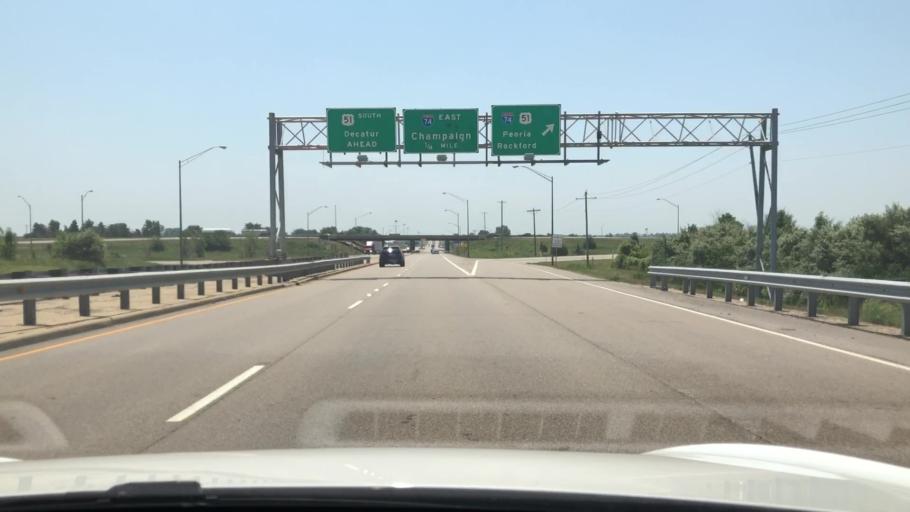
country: US
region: Illinois
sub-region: McLean County
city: Bloomington
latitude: 40.4388
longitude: -88.9908
